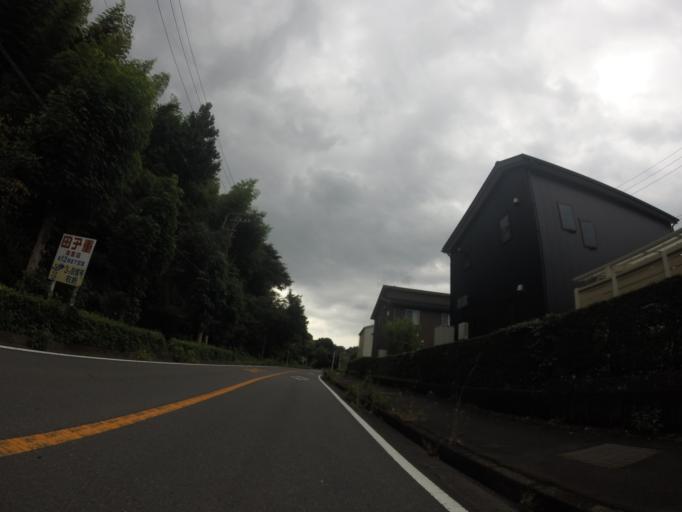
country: JP
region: Shizuoka
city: Fujieda
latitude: 34.8947
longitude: 138.2645
